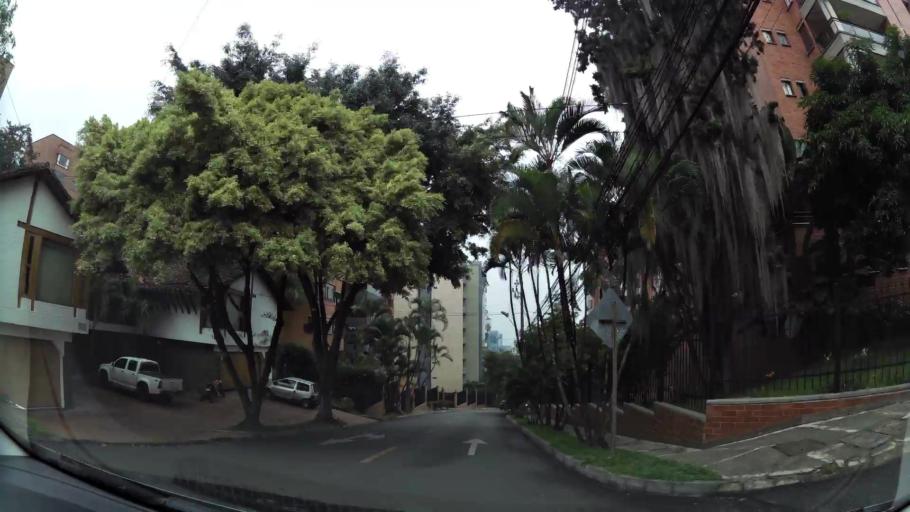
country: CO
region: Antioquia
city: Envigado
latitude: 6.1994
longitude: -75.5691
